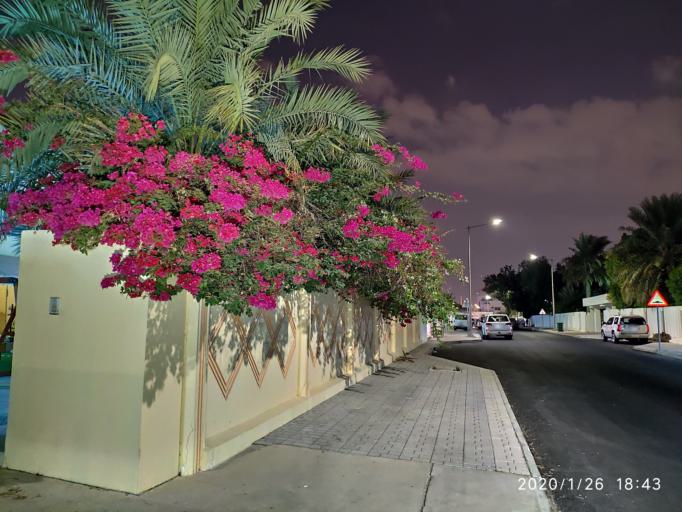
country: QA
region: Baladiyat ad Dawhah
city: Doha
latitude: 25.3253
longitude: 51.5054
